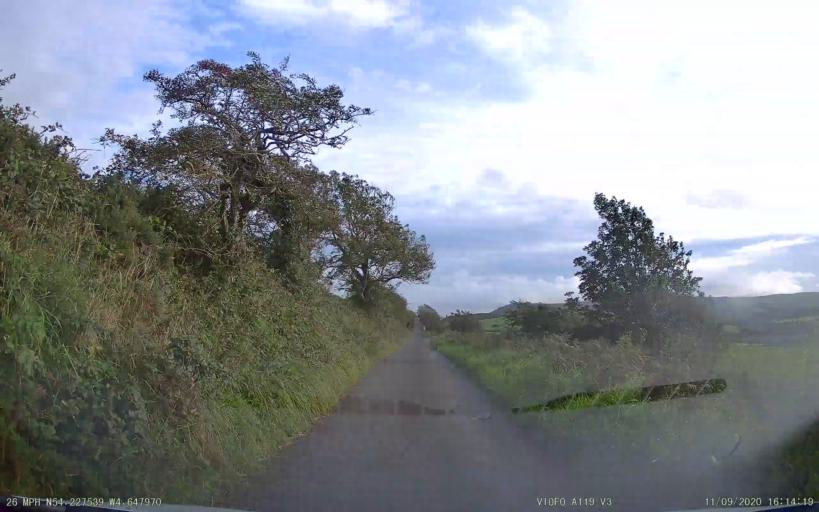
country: IM
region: Castletown
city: Castletown
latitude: 54.2275
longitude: -4.6480
